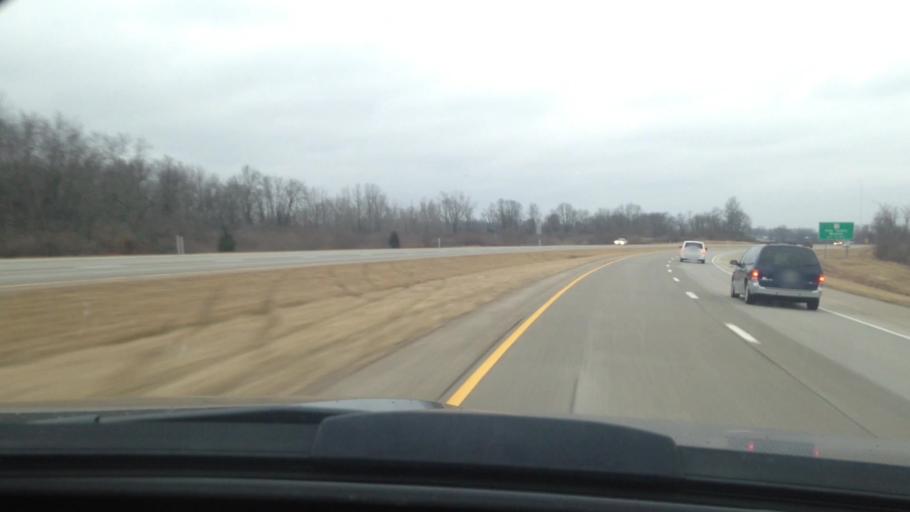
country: US
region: Indiana
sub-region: Delaware County
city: Muncie
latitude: 40.1569
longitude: -85.3535
